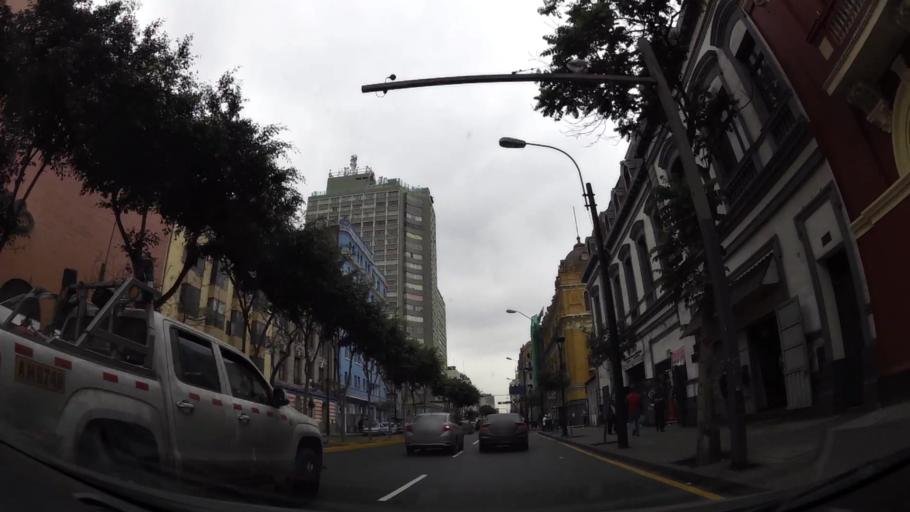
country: PE
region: Lima
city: Lima
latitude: -12.0483
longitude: -77.0398
